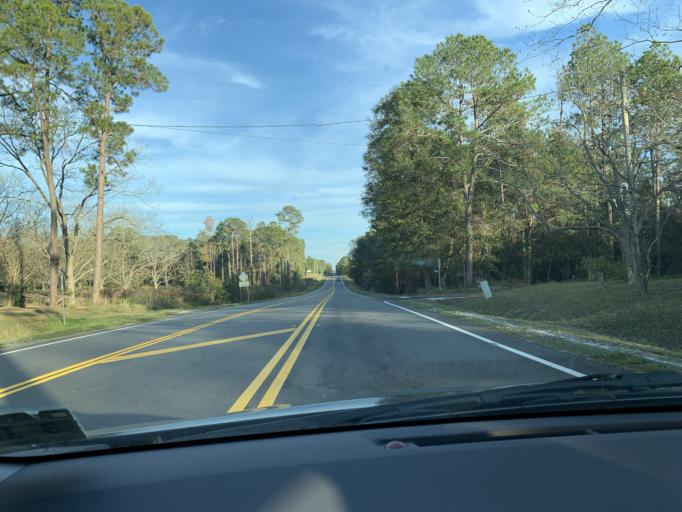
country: US
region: Georgia
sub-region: Irwin County
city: Ocilla
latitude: 31.5958
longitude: -83.1494
